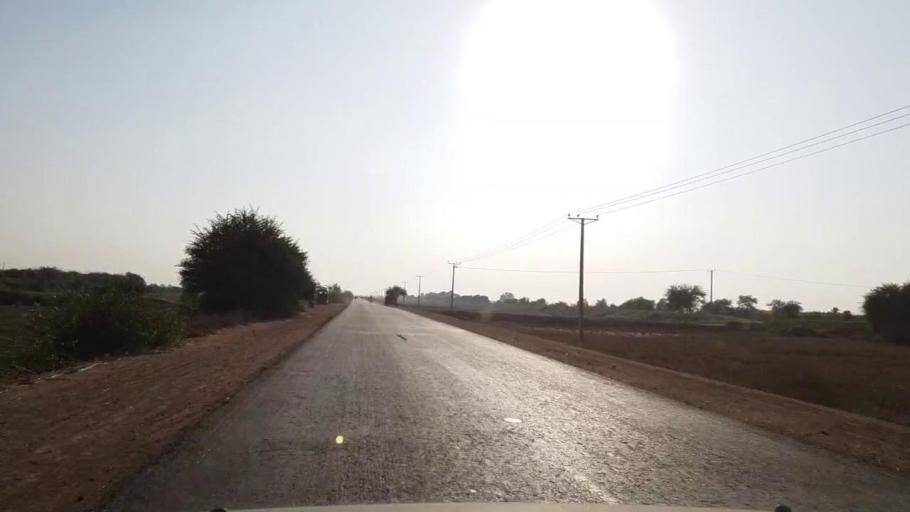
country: PK
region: Sindh
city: Mirpur Batoro
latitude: 24.7696
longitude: 68.2802
